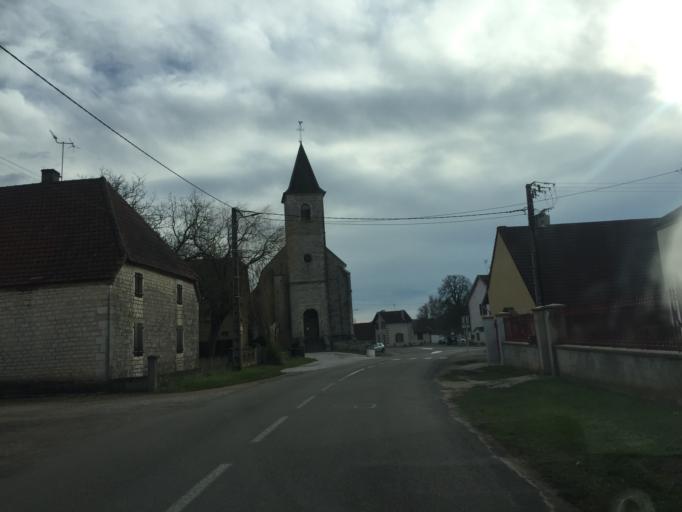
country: FR
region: Franche-Comte
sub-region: Departement du Jura
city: Chaussin
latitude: 46.9159
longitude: 5.4564
